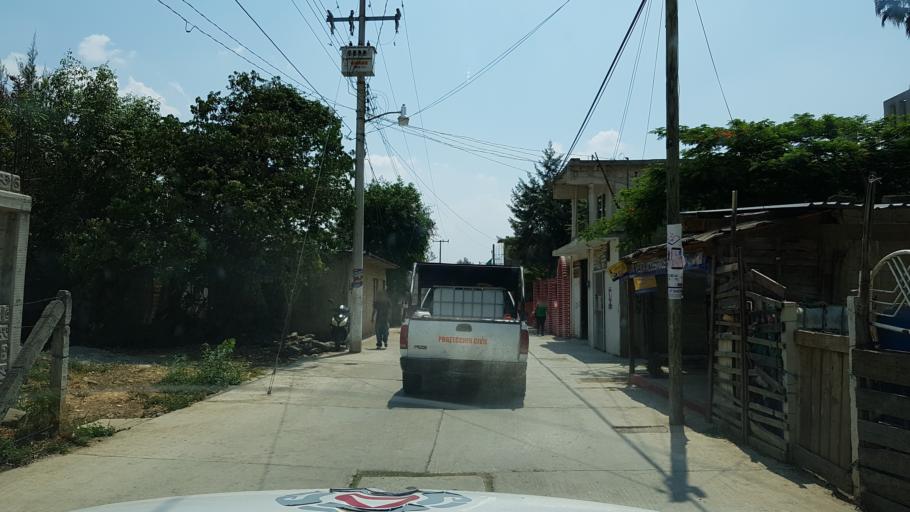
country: MX
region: Morelos
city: Ocuituco
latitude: 18.8845
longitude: -98.8169
